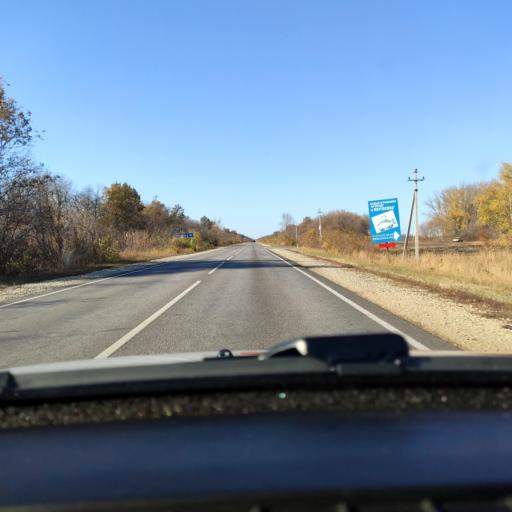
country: RU
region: Voronezj
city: Latnaya
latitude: 51.8044
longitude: 38.8649
